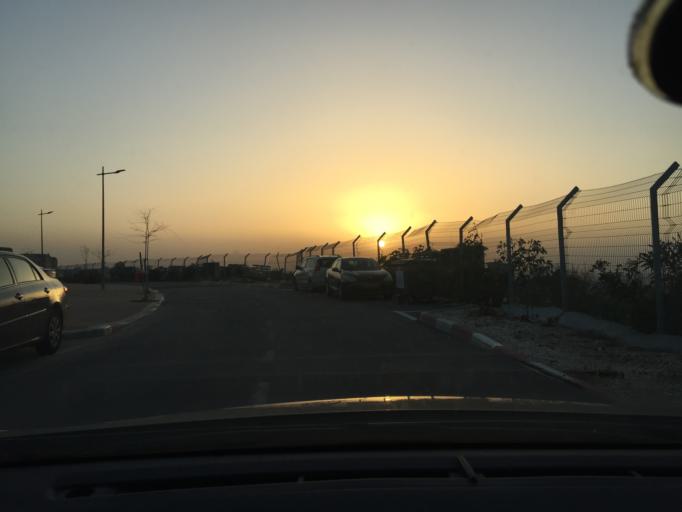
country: PS
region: West Bank
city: Rafat
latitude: 32.0688
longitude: 35.0476
